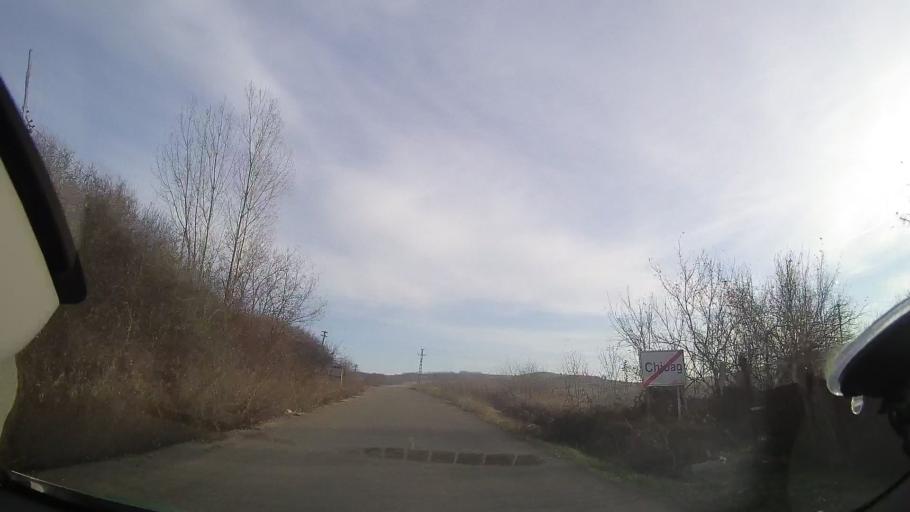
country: RO
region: Bihor
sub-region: Comuna Sarbi
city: Burzuc
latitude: 47.1717
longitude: 22.1562
